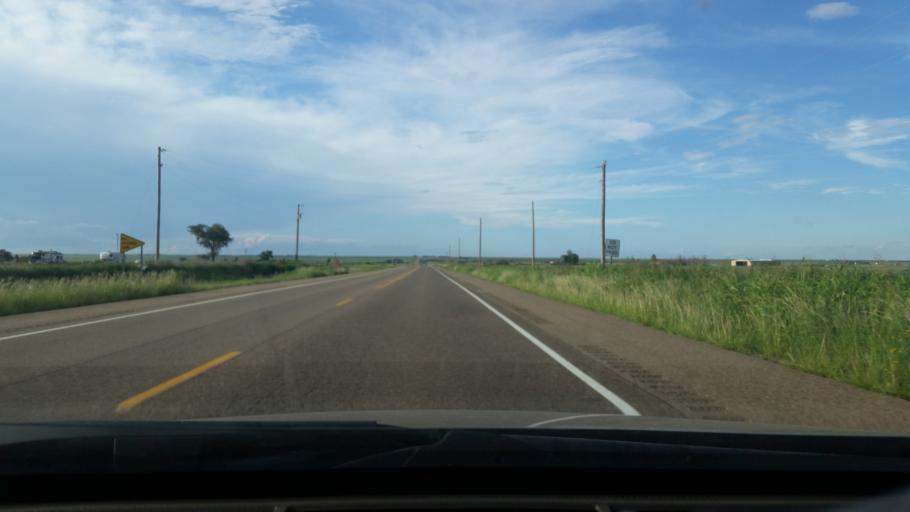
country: US
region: New Mexico
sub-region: Curry County
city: Clovis
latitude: 34.5127
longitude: -103.1962
